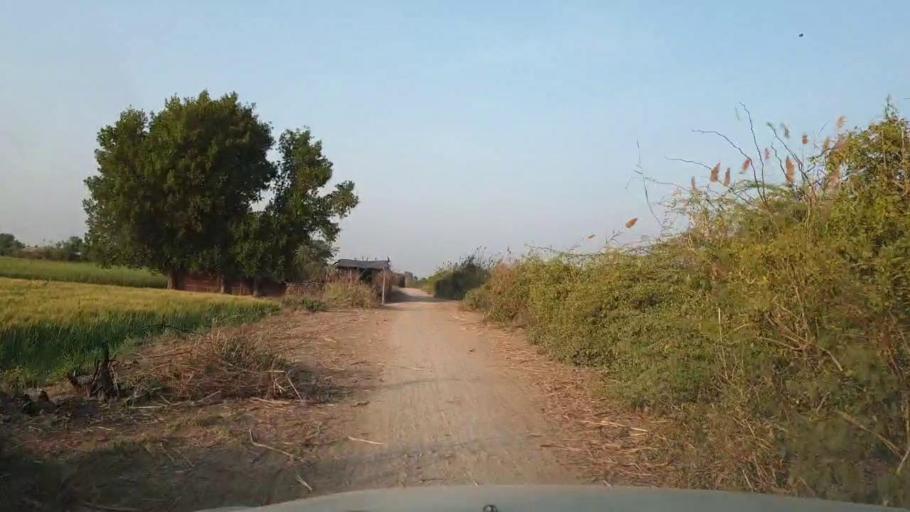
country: PK
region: Sindh
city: Pithoro
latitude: 25.6559
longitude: 69.2130
